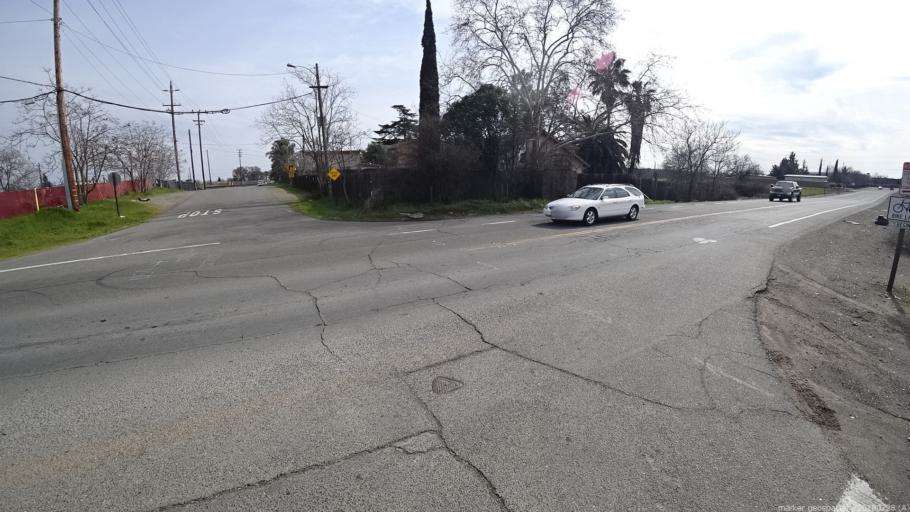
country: US
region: California
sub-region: Sacramento County
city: Antelope
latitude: 38.7094
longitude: -121.3308
